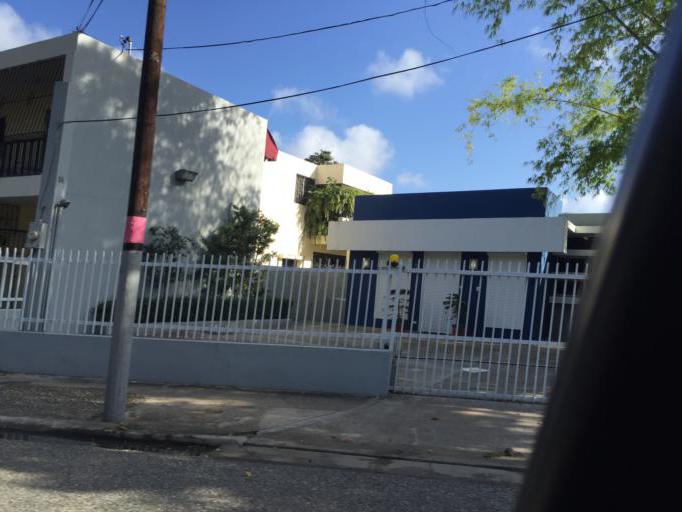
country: DO
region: Nacional
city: La Julia
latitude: 18.4608
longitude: -69.9231
